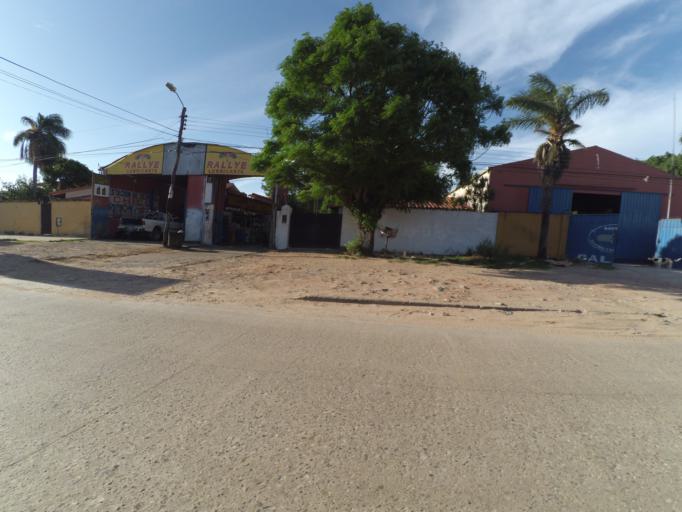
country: BO
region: Santa Cruz
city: Santa Cruz de la Sierra
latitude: -17.7792
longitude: -63.1382
